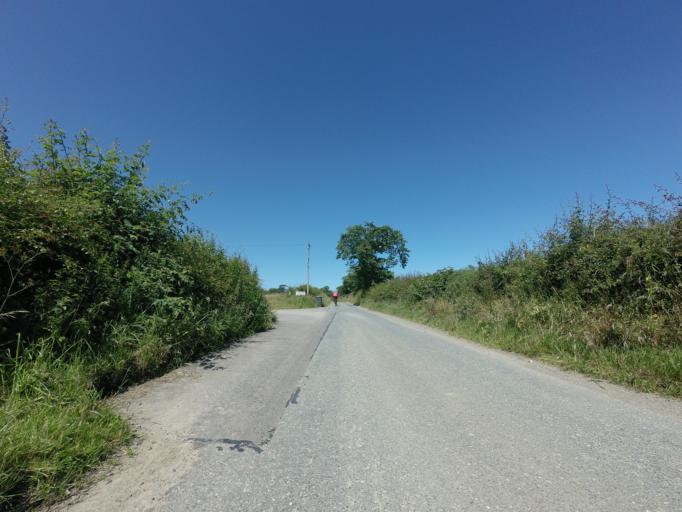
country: GB
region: Scotland
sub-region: Aberdeenshire
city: Macduff
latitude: 57.6354
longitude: -2.4911
